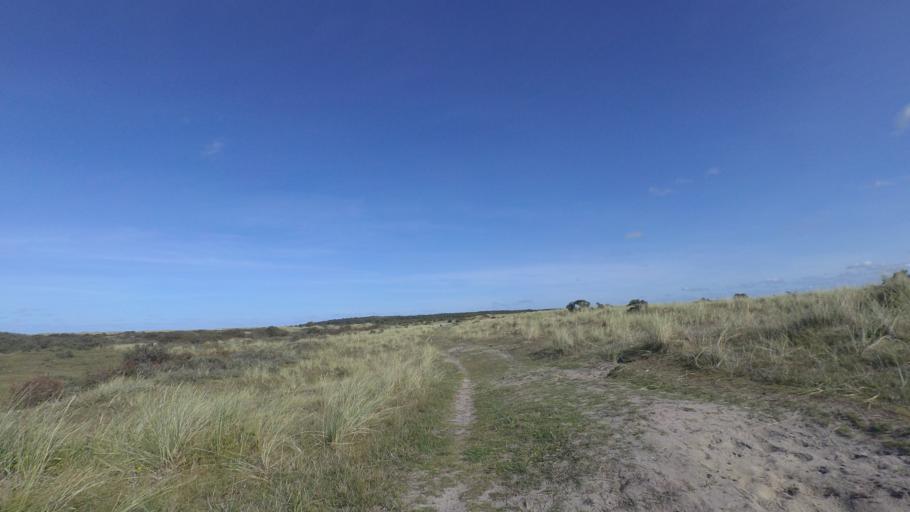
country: NL
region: Friesland
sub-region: Gemeente Ameland
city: Nes
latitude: 53.4500
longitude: 5.7405
